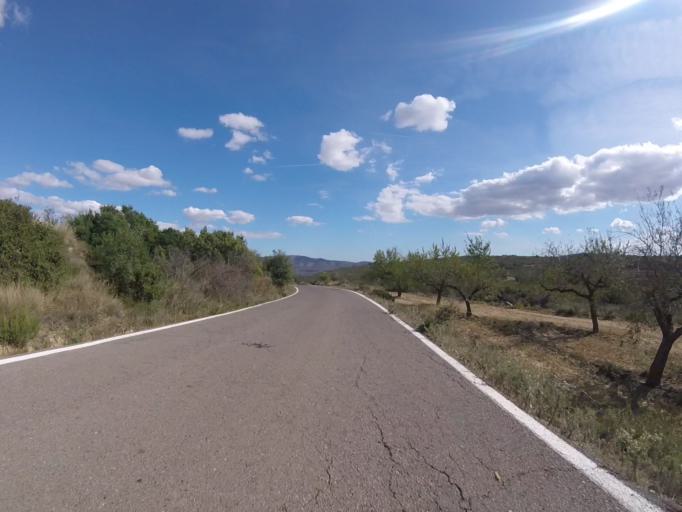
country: ES
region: Valencia
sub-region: Provincia de Castello
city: Albocasser
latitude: 40.3953
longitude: 0.0915
